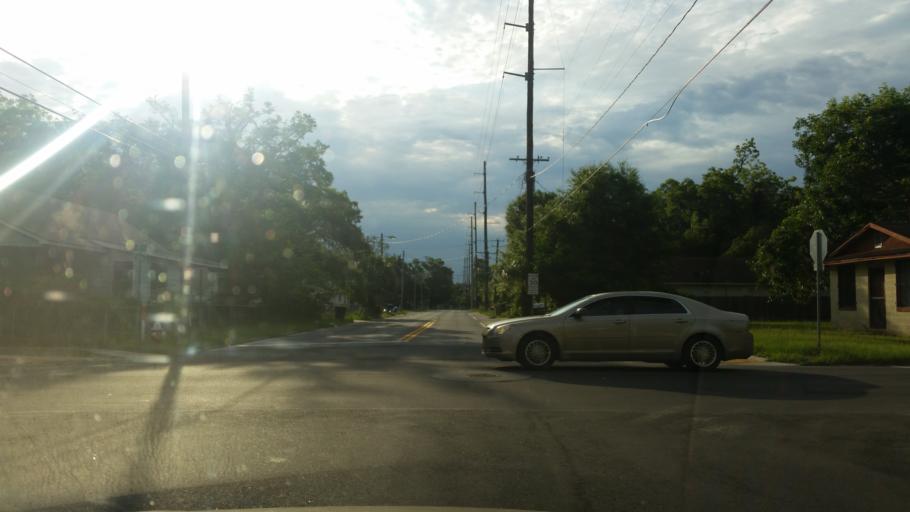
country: US
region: Florida
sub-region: Escambia County
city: Pensacola
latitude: 30.4182
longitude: -87.2304
